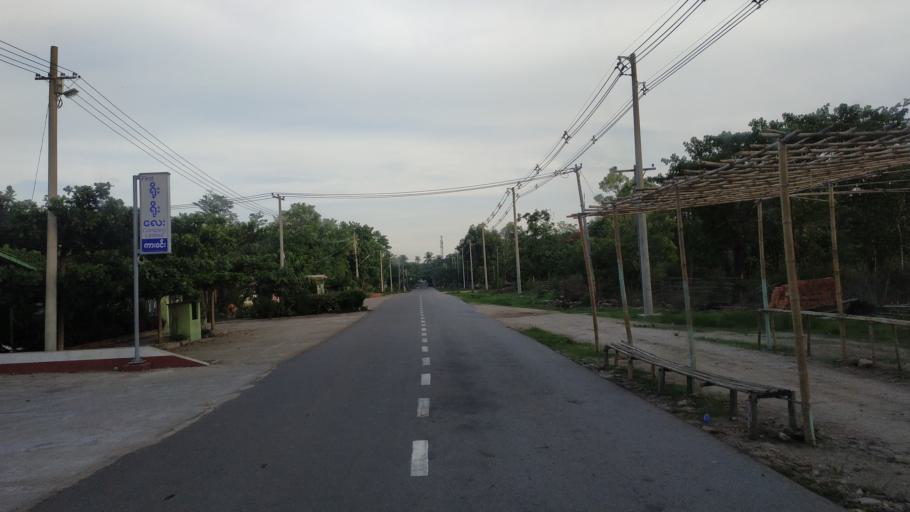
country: MM
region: Mon
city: Kyaikto
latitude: 17.4080
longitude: 97.0733
